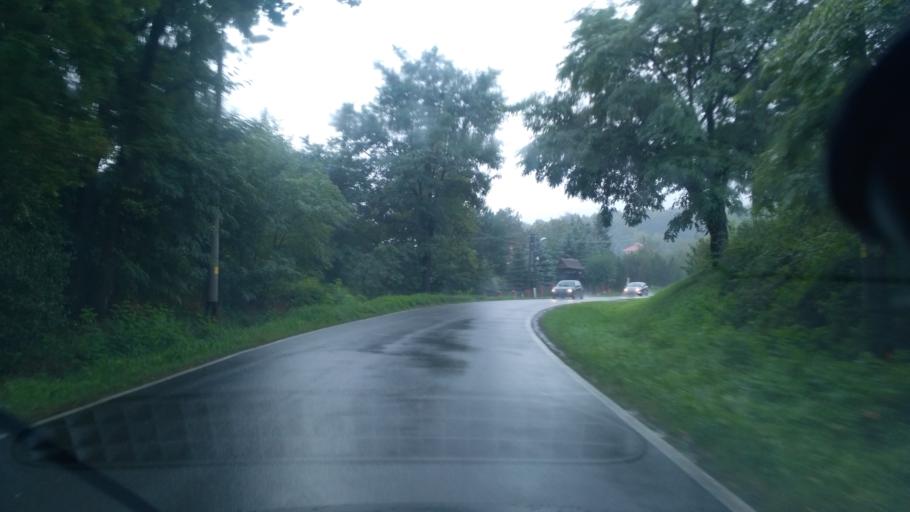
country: PL
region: Subcarpathian Voivodeship
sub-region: Powiat debicki
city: Brzeznica
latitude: 50.0605
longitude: 21.5346
